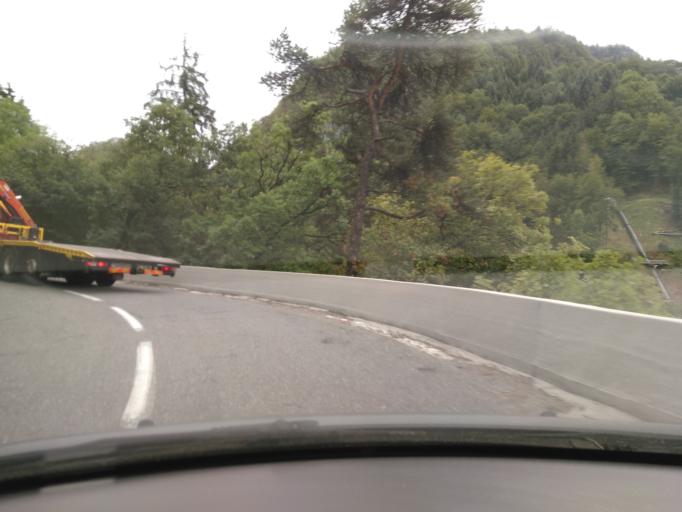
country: FR
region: Rhone-Alpes
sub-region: Departement de la Haute-Savoie
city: Bonneville
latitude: 46.0467
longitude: 6.3757
